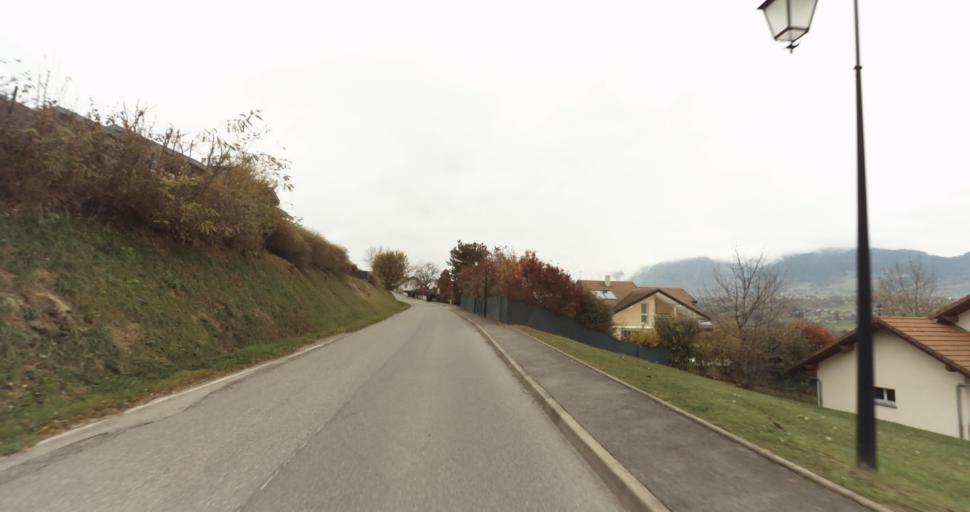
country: FR
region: Rhone-Alpes
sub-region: Departement de la Haute-Savoie
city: Saint-Martin-Bellevue
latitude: 45.9491
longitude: 6.1532
